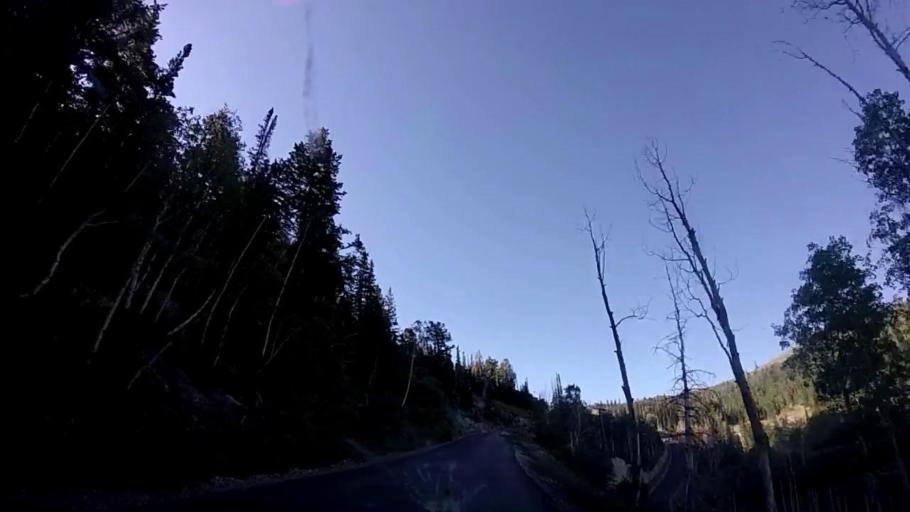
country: US
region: Utah
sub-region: Summit County
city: Park City
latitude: 40.6142
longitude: -111.5068
